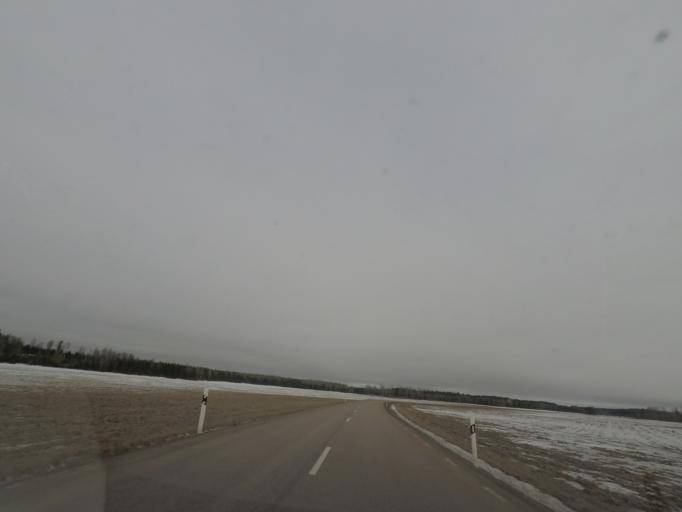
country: SE
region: Vaestmanland
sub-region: Vasteras
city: Skultuna
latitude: 59.7318
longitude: 16.4163
